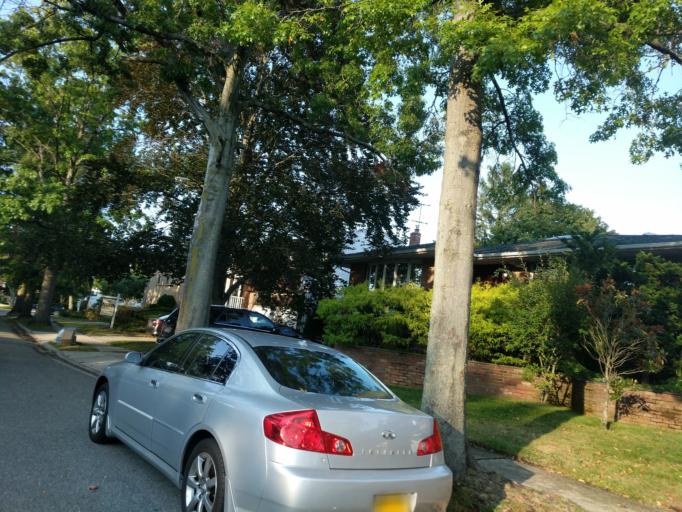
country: US
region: New York
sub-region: Nassau County
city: South Valley Stream
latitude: 40.6438
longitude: -73.7247
